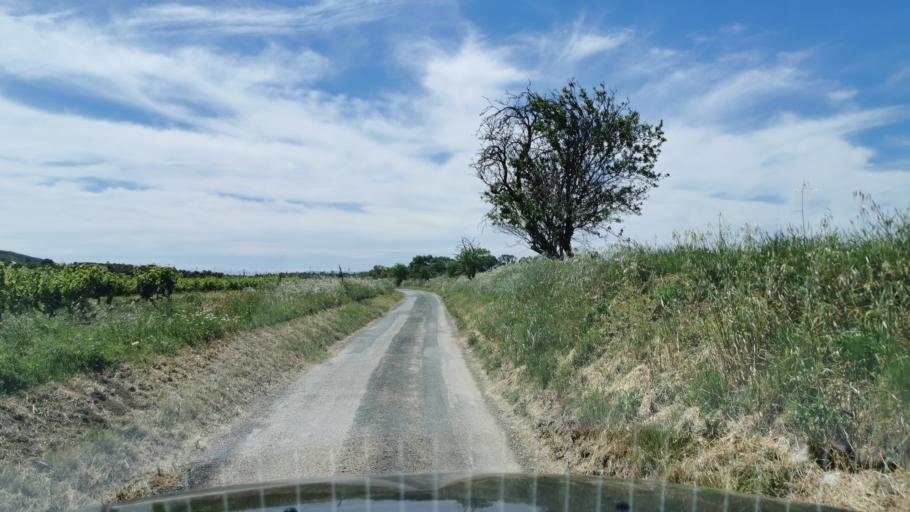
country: FR
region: Languedoc-Roussillon
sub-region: Departement de l'Aude
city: Nevian
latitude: 43.2170
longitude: 2.8887
